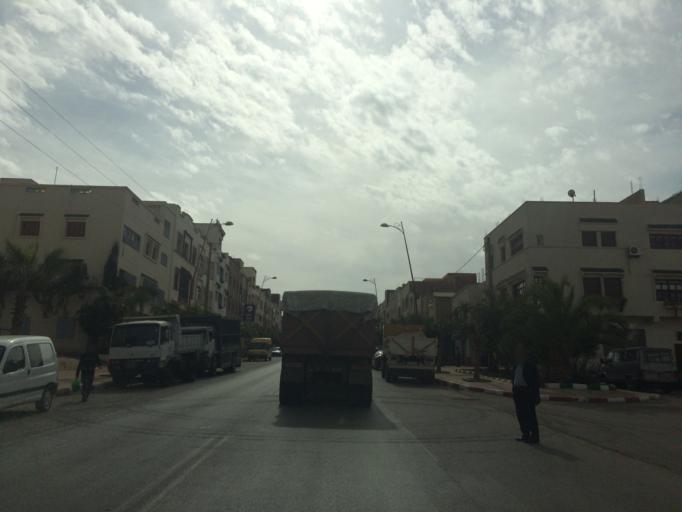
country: MA
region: Meknes-Tafilalet
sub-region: El-Hajeb
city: El Hajeb
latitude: 33.7571
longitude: -5.4850
